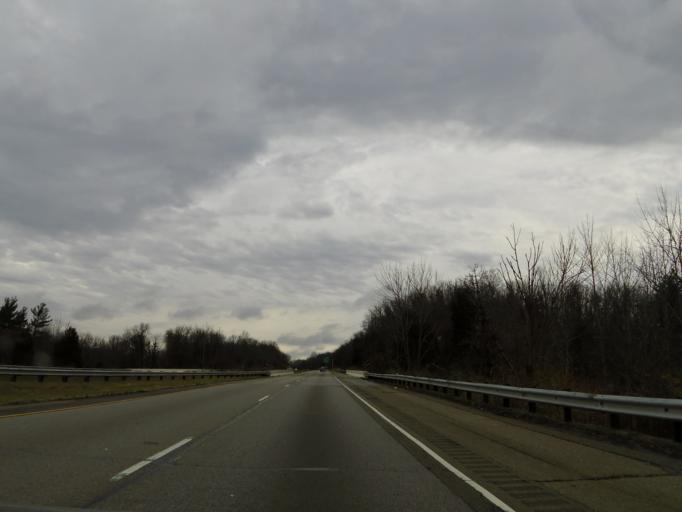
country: US
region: Ohio
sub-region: Hamilton County
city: Grandview
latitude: 39.2353
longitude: -84.7619
